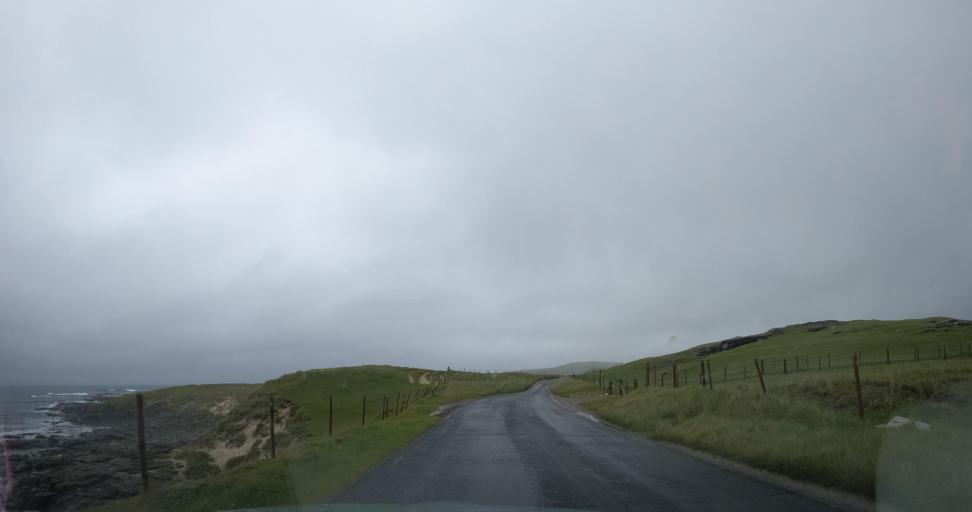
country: GB
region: Scotland
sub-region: Eilean Siar
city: Barra
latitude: 56.9941
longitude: -7.5073
